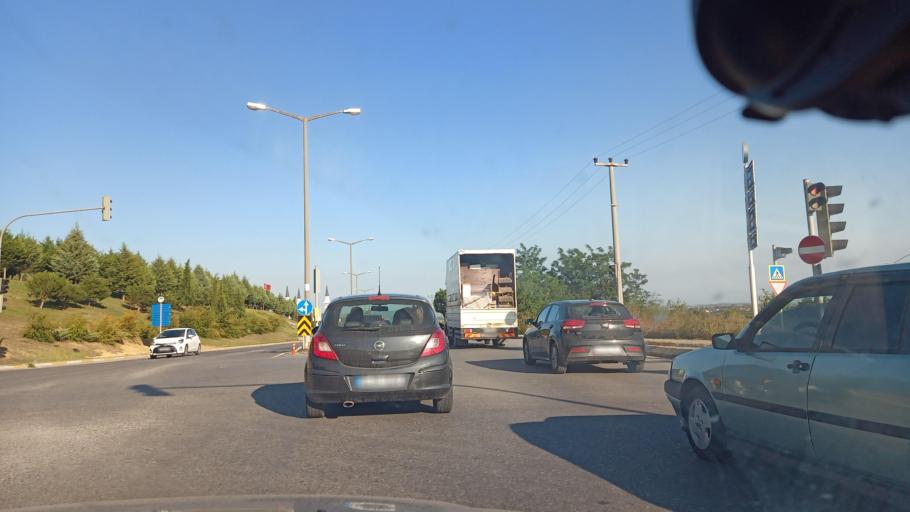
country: TR
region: Sakarya
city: Kazimpasa
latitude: 40.8528
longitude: 30.3072
